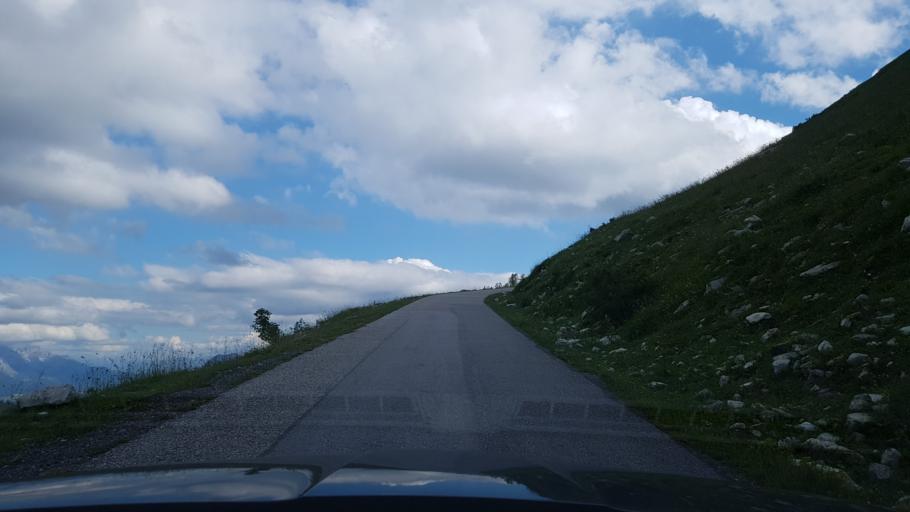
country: AT
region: Salzburg
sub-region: Politischer Bezirk Salzburg-Umgebung
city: Hintersee
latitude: 47.6429
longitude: 13.2789
